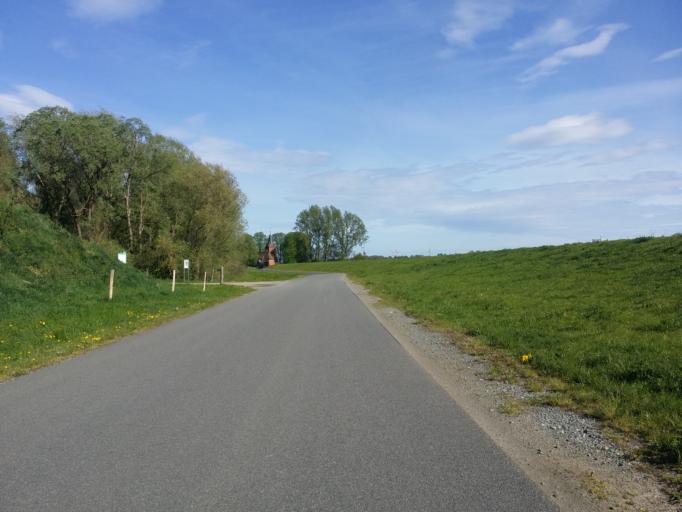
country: DE
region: Lower Saxony
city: Lemwerder
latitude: 53.1299
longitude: 8.6484
